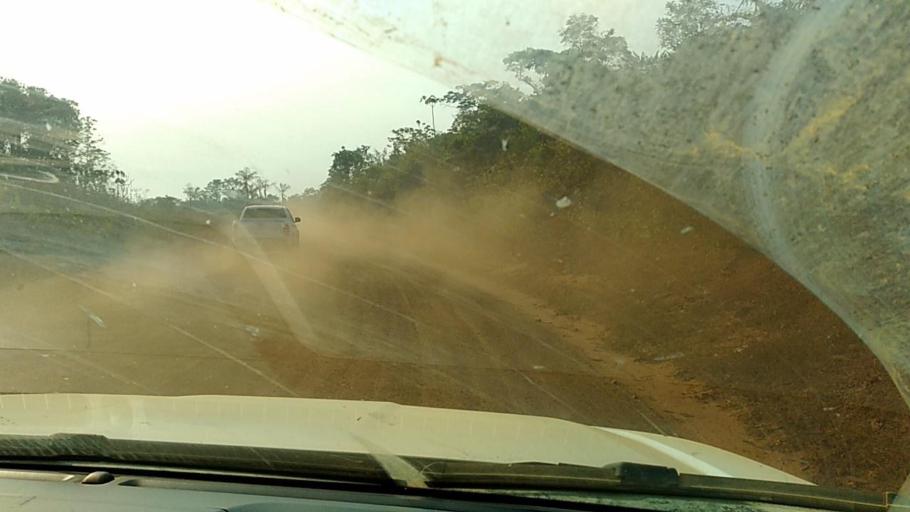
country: BR
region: Rondonia
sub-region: Porto Velho
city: Porto Velho
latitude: -8.7395
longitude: -63.9686
